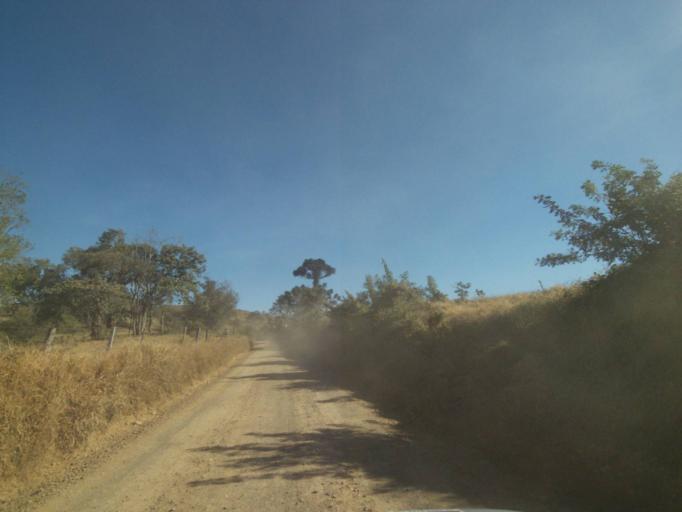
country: BR
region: Parana
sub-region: Tibagi
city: Tibagi
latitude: -24.5374
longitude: -50.4668
